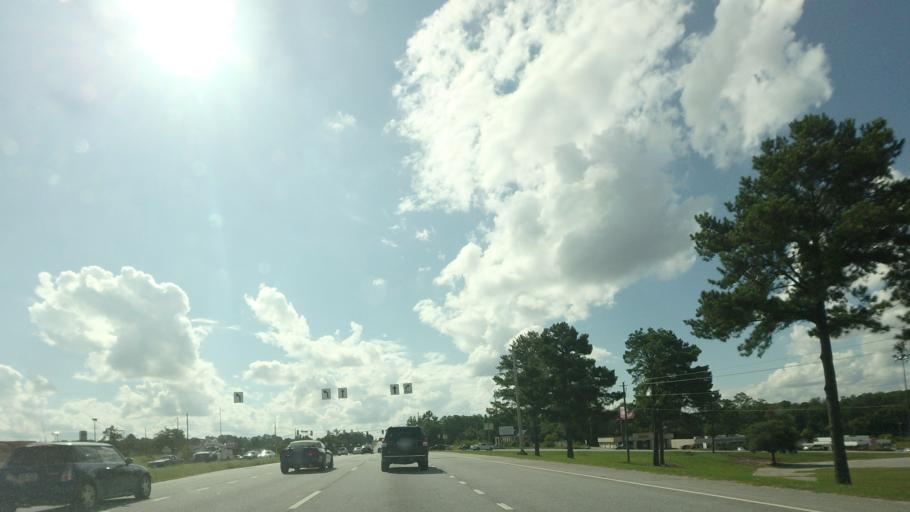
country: US
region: Georgia
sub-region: Bibb County
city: Macon
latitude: 32.8160
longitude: -83.6970
